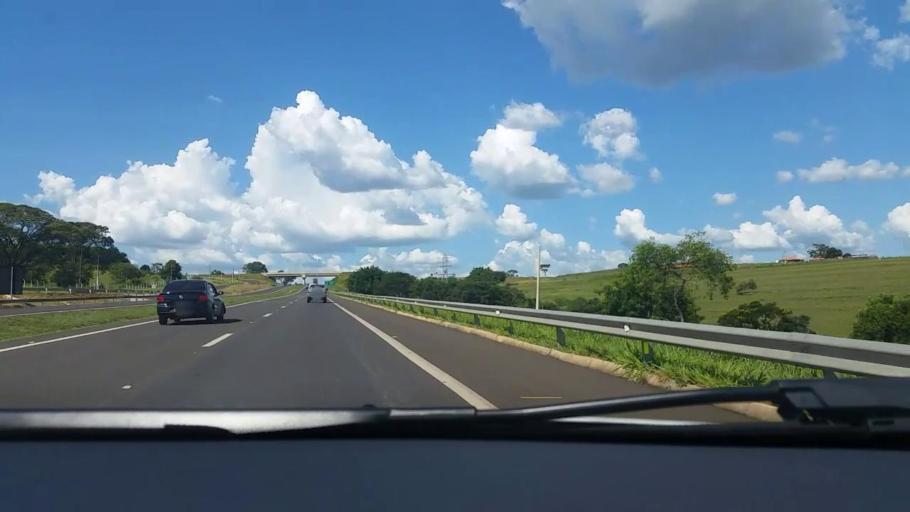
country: BR
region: Sao Paulo
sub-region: Bauru
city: Bauru
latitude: -22.4022
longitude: -49.0921
